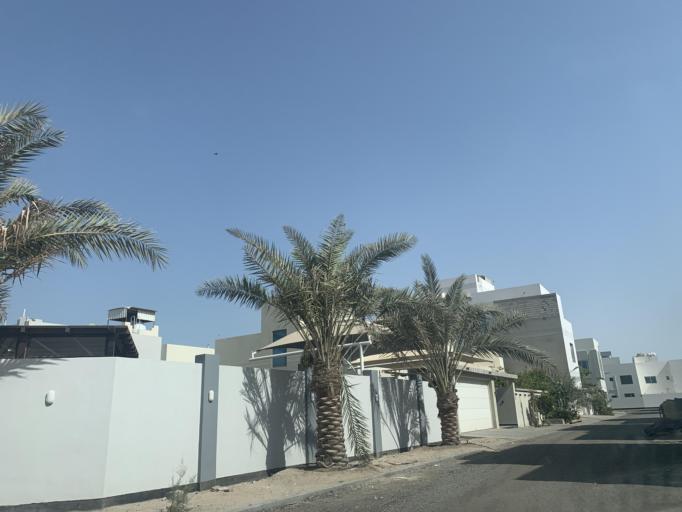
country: BH
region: Manama
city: Jidd Hafs
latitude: 26.2356
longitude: 50.5076
